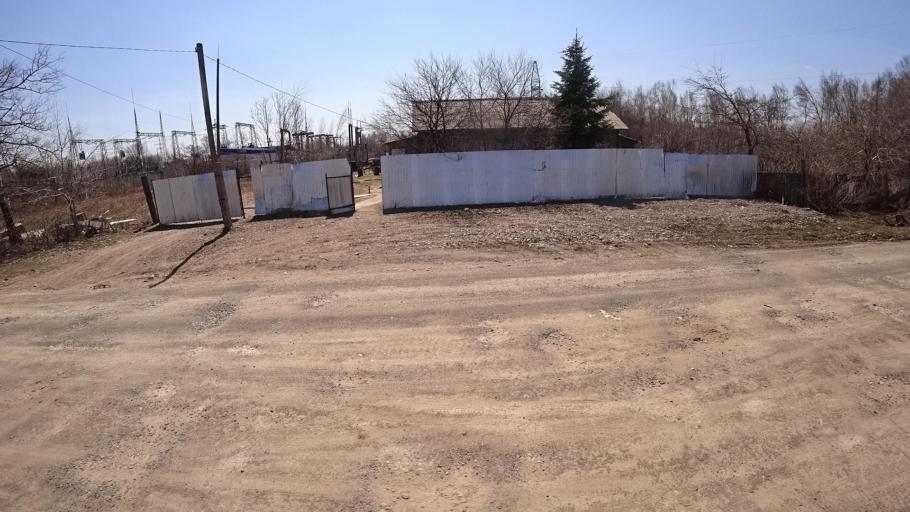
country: RU
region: Khabarovsk Krai
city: Khurba
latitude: 50.4096
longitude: 136.8578
